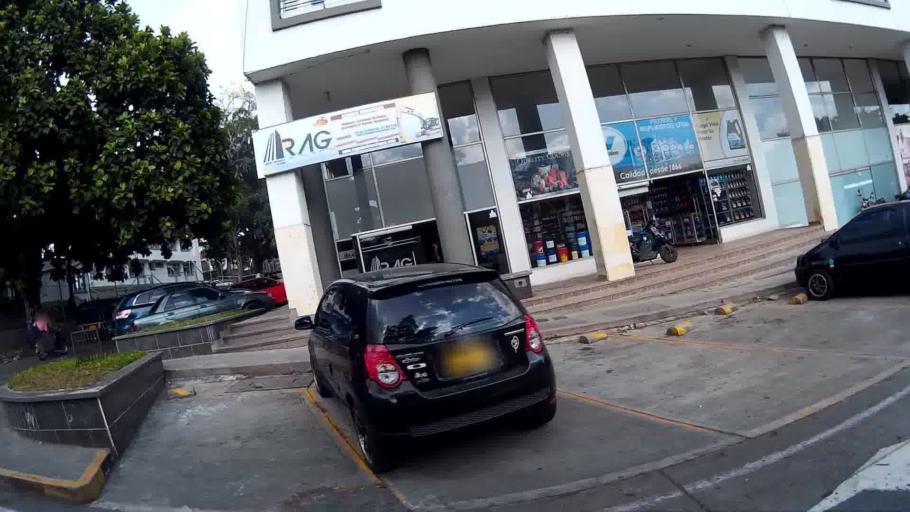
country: CO
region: Quindio
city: Armenia
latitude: 4.5409
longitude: -75.6692
